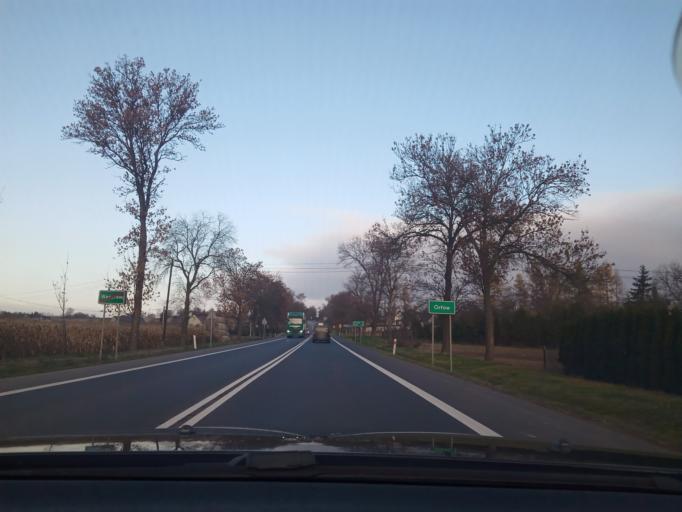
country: PL
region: Lesser Poland Voivodeship
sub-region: Powiat krakowski
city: Slomniki
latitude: 50.2866
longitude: 20.0519
